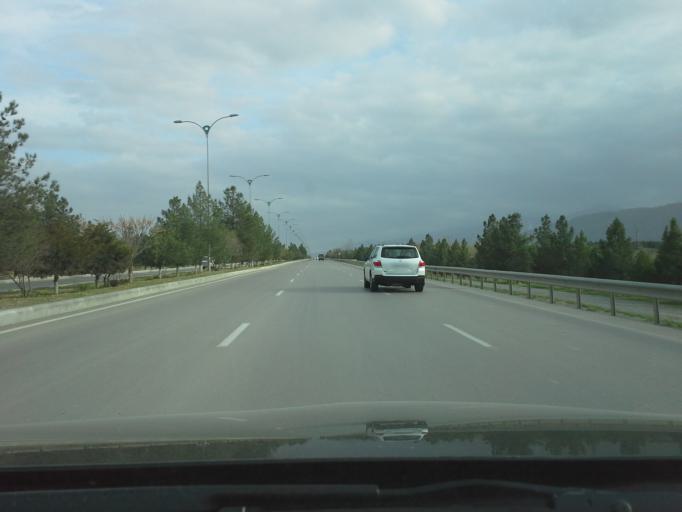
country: TM
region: Ahal
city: Abadan
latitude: 37.9553
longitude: 58.2265
